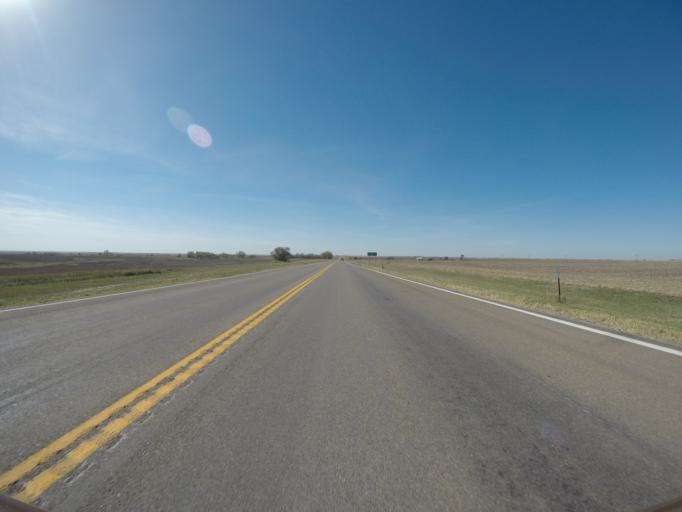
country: US
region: Kansas
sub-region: Smith County
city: Smith Center
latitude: 39.7710
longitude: -98.9366
